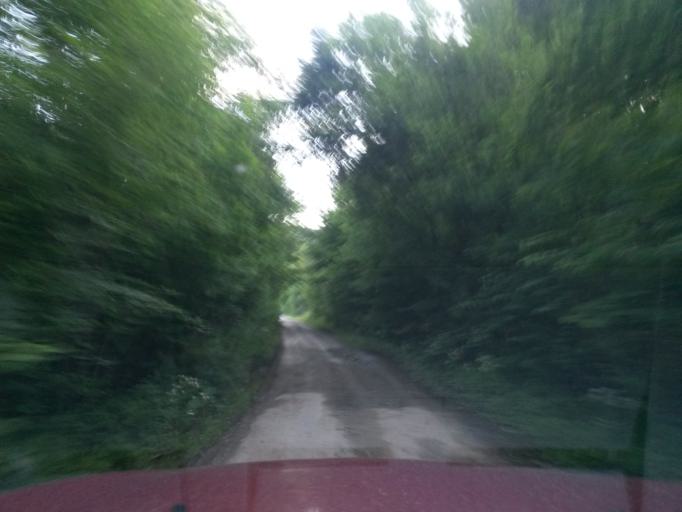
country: UA
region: Zakarpattia
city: Velykyi Bereznyi
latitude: 48.8513
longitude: 22.3637
